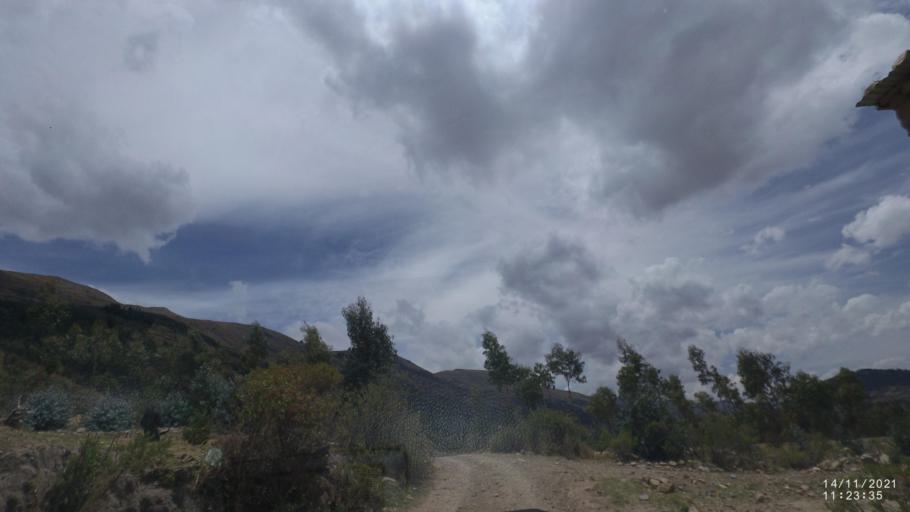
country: BO
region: Cochabamba
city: Cochabamba
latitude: -17.3348
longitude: -66.0293
